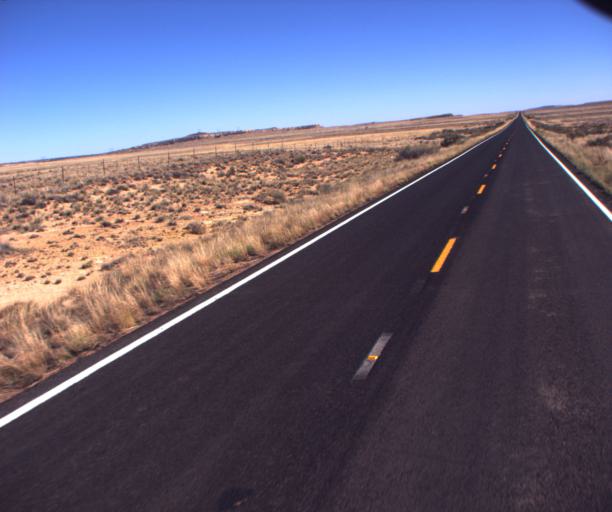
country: US
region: Arizona
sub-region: Navajo County
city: First Mesa
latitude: 35.9714
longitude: -110.7876
